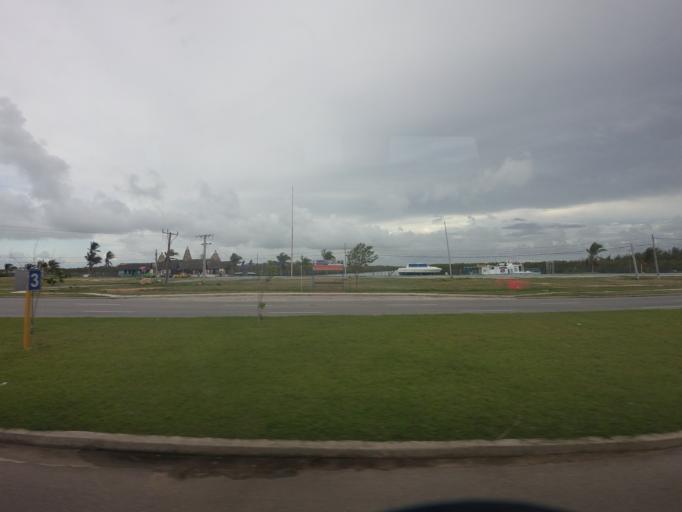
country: CU
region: Matanzas
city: Varadero
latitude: 23.1846
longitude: -81.1749
